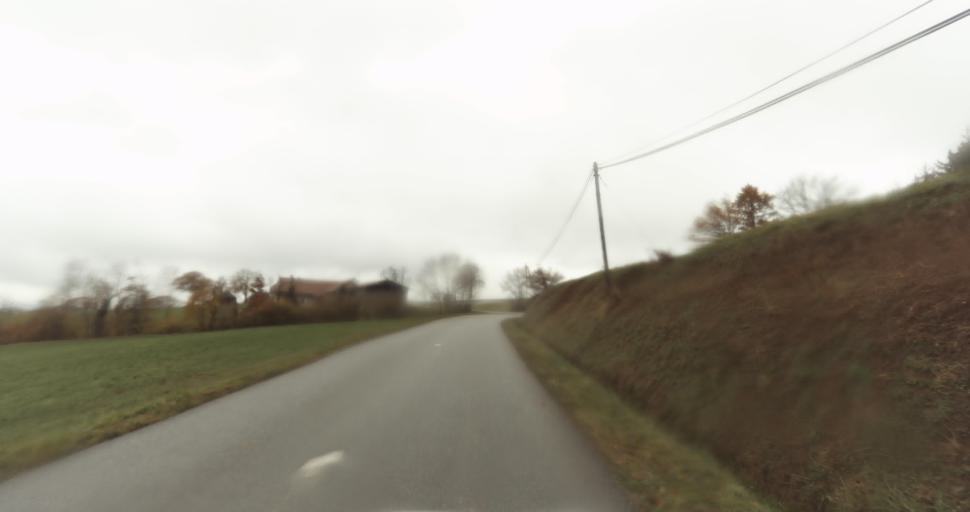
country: FR
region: Rhone-Alpes
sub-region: Departement de la Haute-Savoie
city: Thorens-Glieres
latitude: 46.0073
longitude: 6.2387
